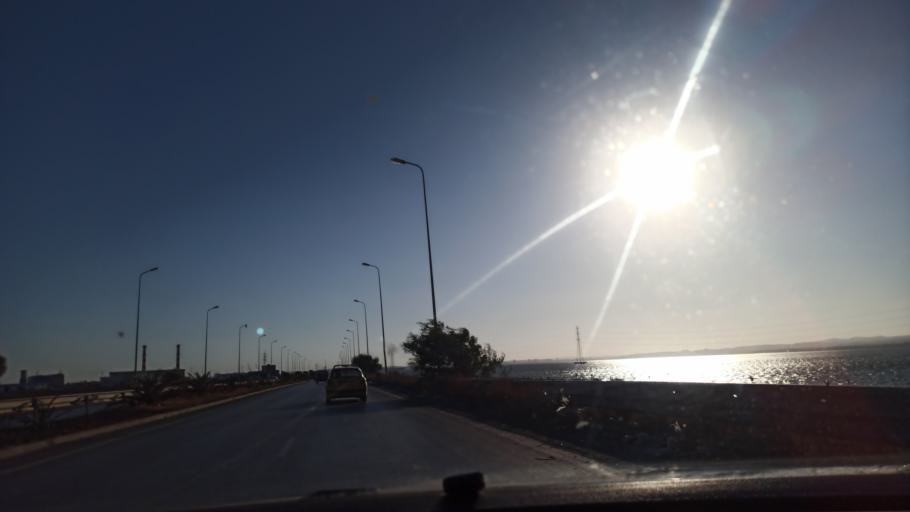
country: TN
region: Tunis
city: La Goulette
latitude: 36.8223
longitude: 10.2983
